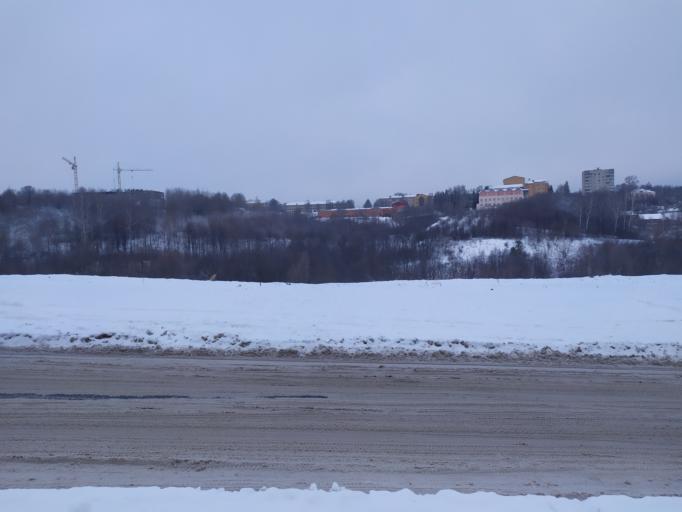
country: RU
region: Chuvashia
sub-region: Cheboksarskiy Rayon
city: Cheboksary
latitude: 56.1199
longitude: 47.2086
